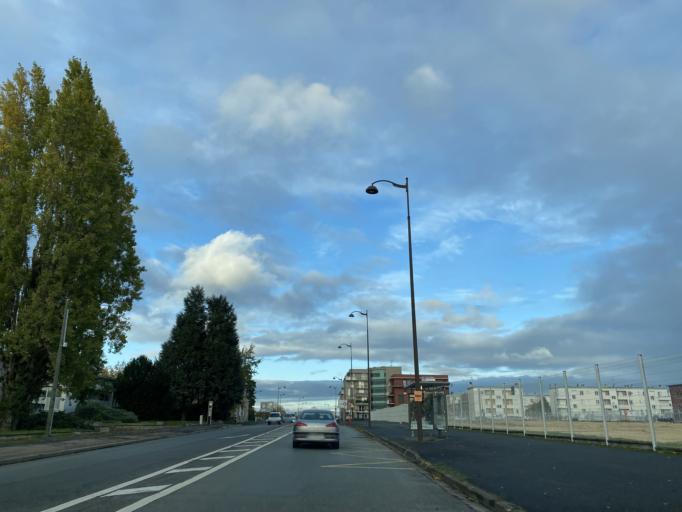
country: FR
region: Centre
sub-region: Departement du Cher
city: Bourges
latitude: 47.0675
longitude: 2.3729
